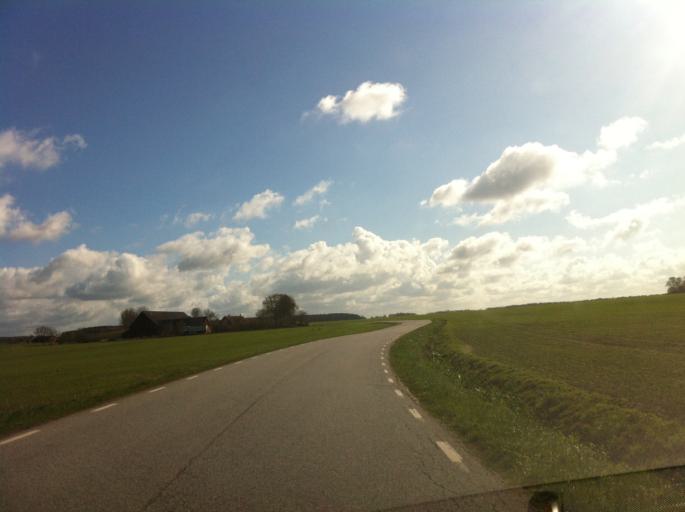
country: SE
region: Skane
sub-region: Eslovs Kommun
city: Eslov
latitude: 55.8663
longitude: 13.2424
